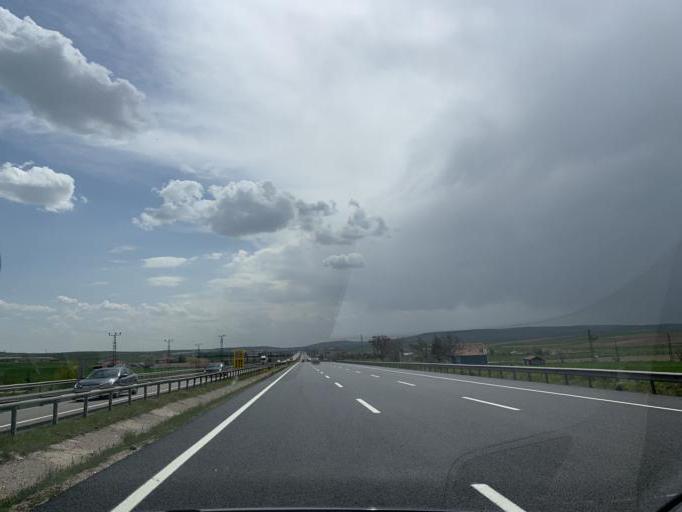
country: TR
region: Ankara
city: Polatli
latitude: 39.6678
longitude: 32.2286
